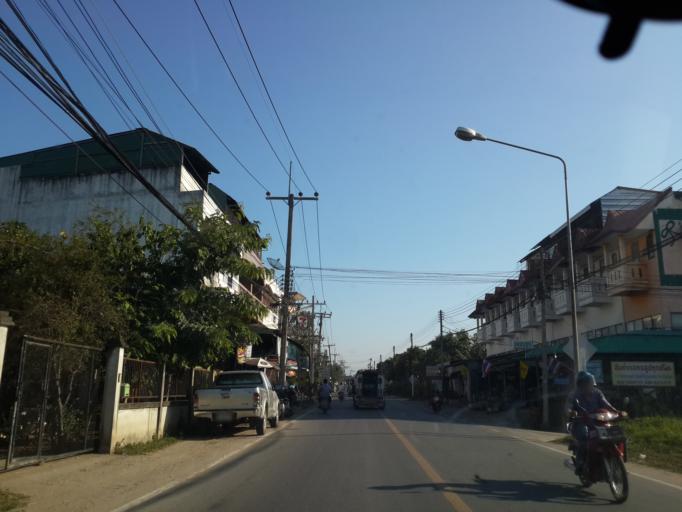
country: TH
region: Chiang Mai
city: San Kamphaeng
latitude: 18.7352
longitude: 99.1268
